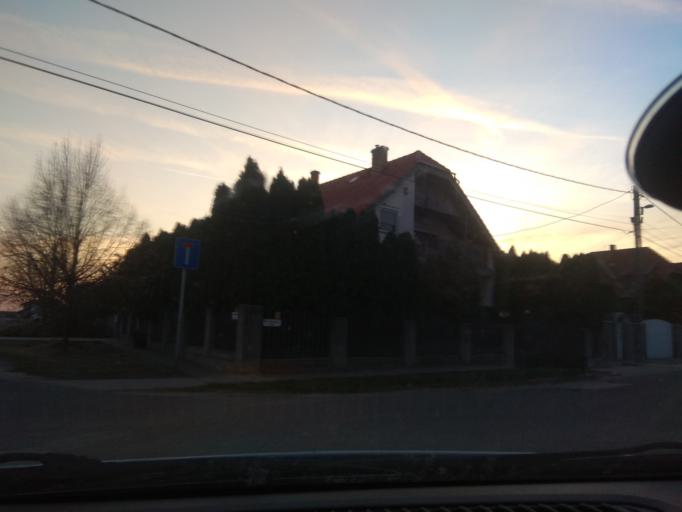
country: HU
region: Pest
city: Szigetszentmiklos
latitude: 47.3477
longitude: 19.0302
